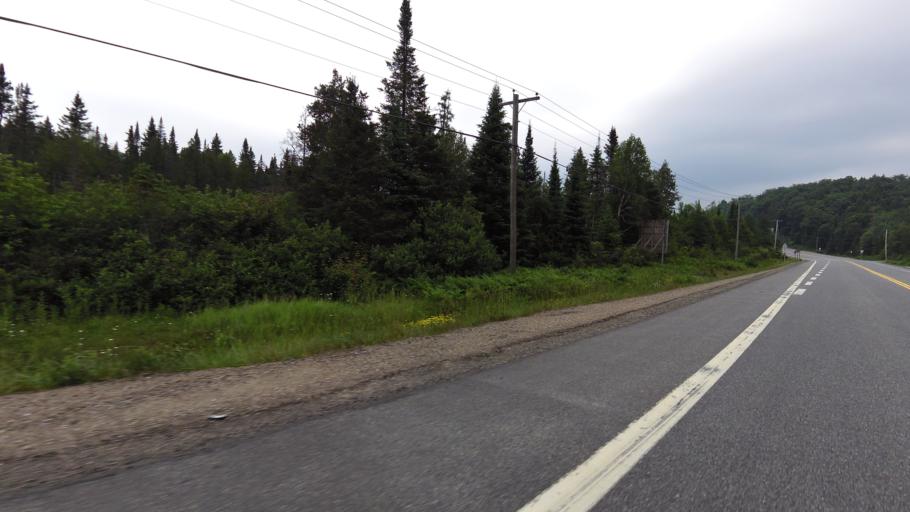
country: CA
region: Ontario
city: Huntsville
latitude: 45.4050
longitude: -78.8756
